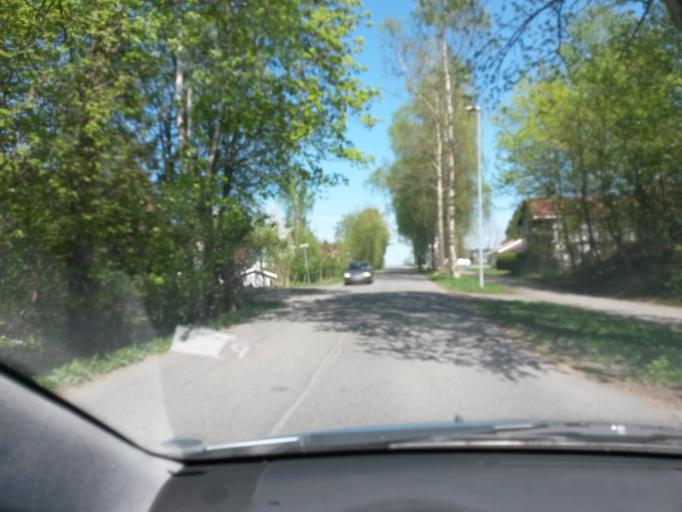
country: NO
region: Akershus
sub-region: Asker
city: Asker
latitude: 59.8315
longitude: 10.4075
